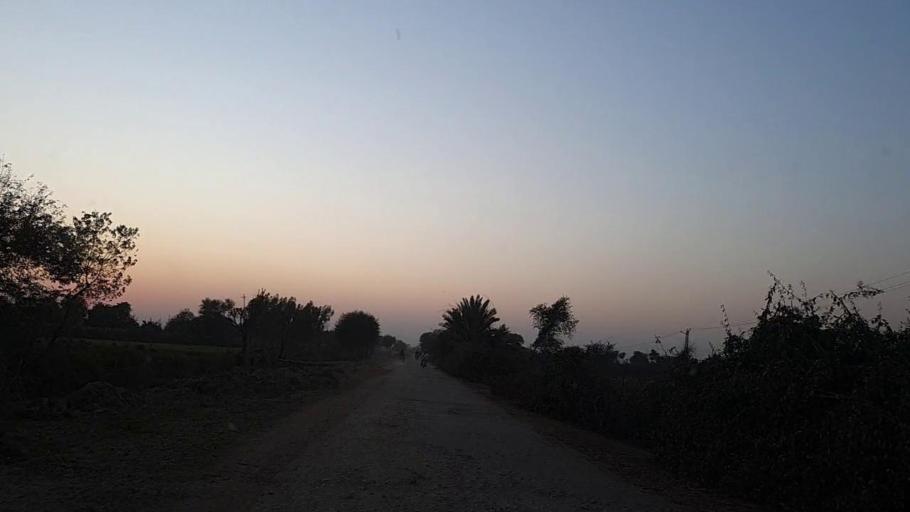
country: PK
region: Sindh
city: Hala
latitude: 25.9599
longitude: 68.3984
